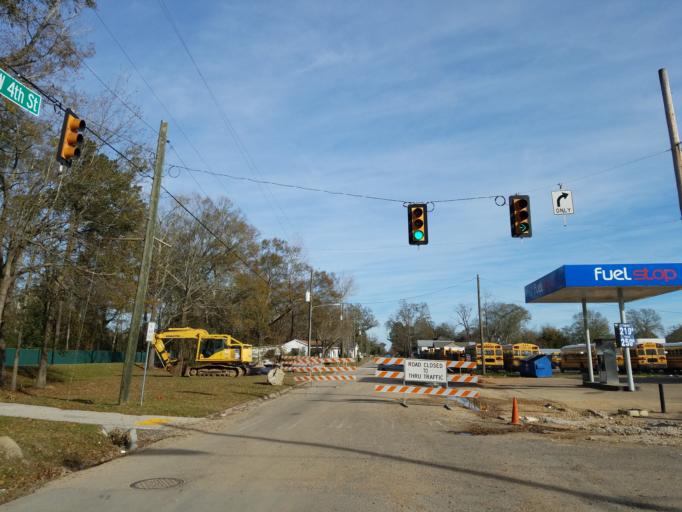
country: US
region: Mississippi
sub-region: Forrest County
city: Hattiesburg
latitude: 31.3320
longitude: -89.3100
